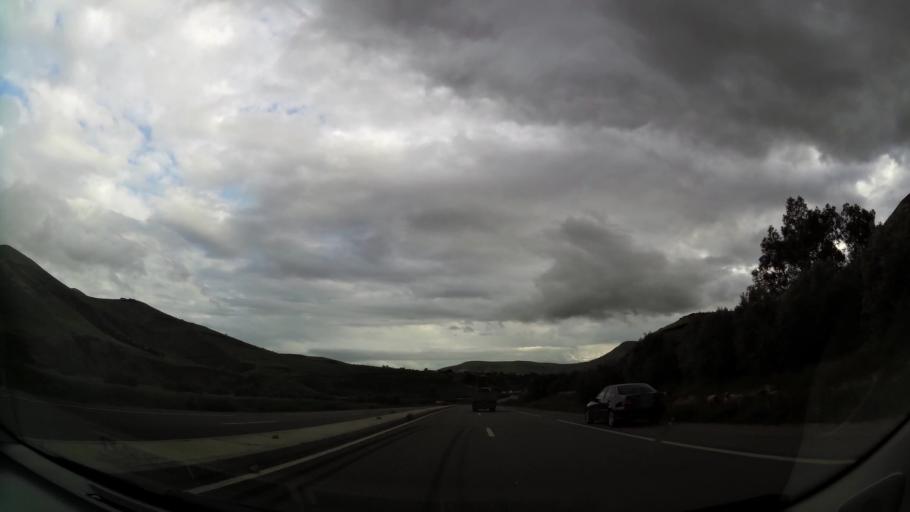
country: MA
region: Taza-Al Hoceima-Taounate
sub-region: Taza
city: Taza
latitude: 34.3167
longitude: -3.9595
